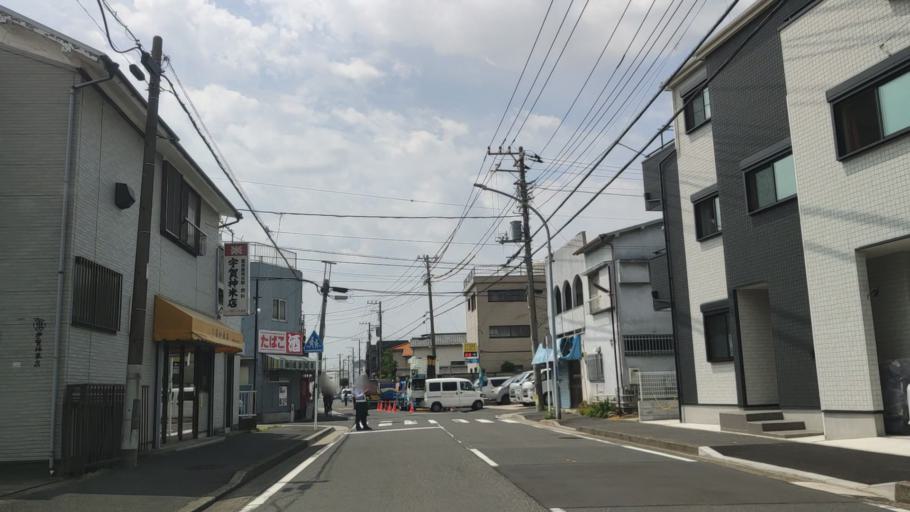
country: JP
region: Kanagawa
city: Yokohama
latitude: 35.4186
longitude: 139.6237
